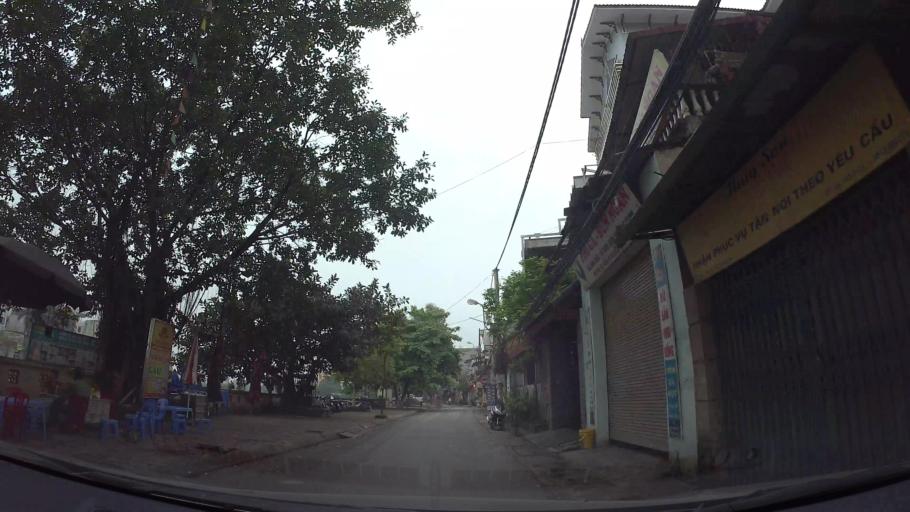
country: VN
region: Ha Noi
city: Van Dien
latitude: 20.9689
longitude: 105.8713
